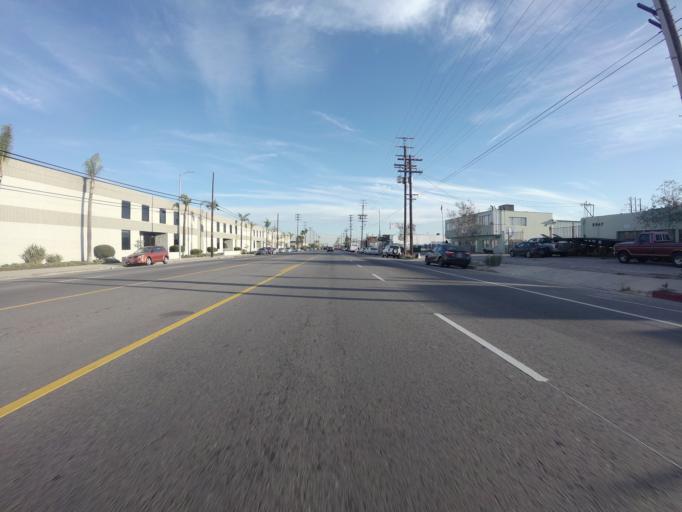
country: US
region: California
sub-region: Los Angeles County
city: San Fernando
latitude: 34.2488
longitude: -118.3865
